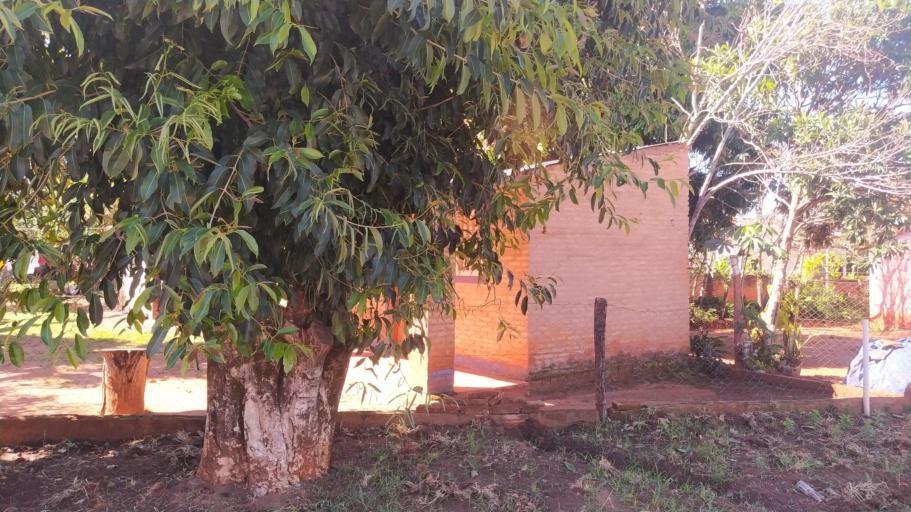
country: PY
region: Misiones
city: San Juan Bautista
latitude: -26.6777
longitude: -57.1441
